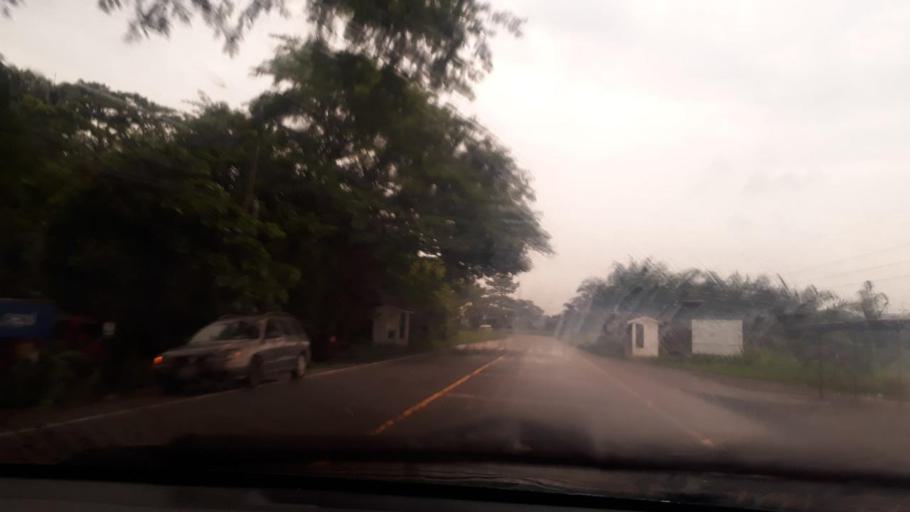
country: GT
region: Escuintla
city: Guanagazapa
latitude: 14.1136
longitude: -90.6348
